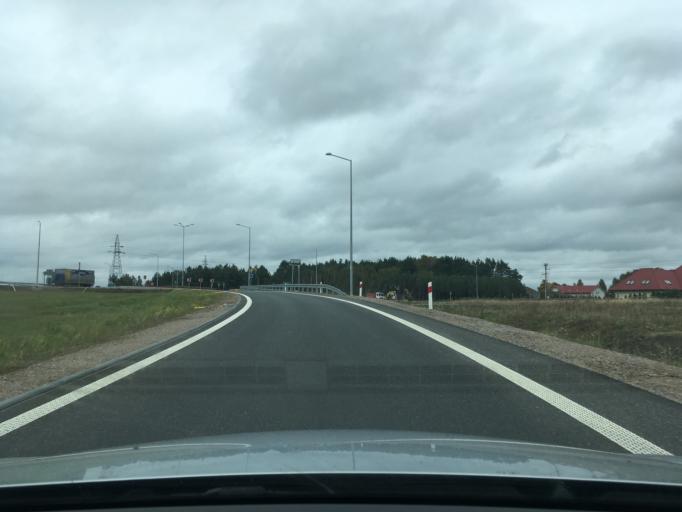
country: PL
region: Pomeranian Voivodeship
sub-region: Powiat koscierski
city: Koscierzyna
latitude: 54.1221
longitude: 18.0196
